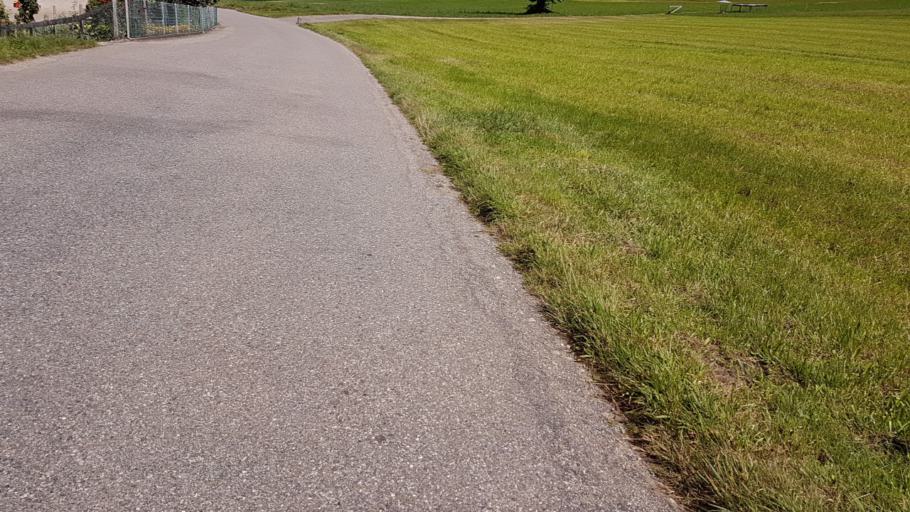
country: CH
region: Lucerne
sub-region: Entlebuch District
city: Oberdiessbach
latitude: 46.8519
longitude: 7.6227
